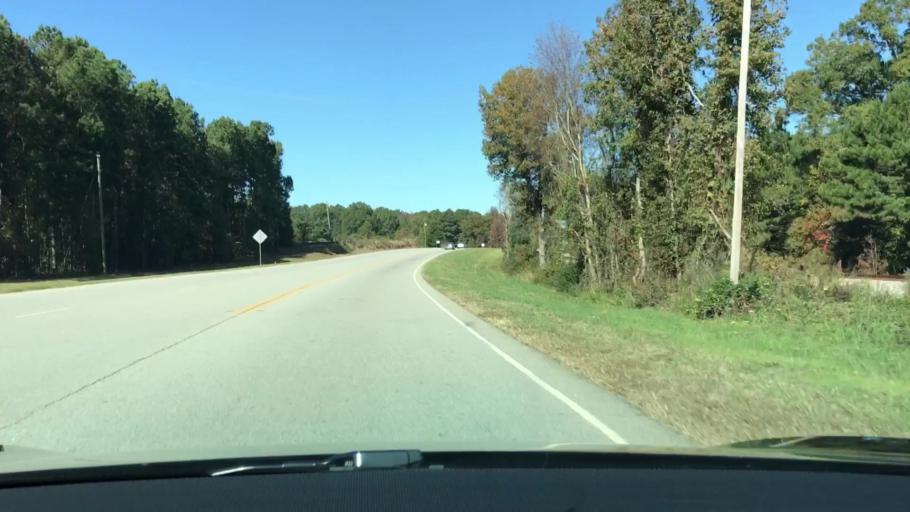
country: US
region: Georgia
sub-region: Warren County
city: Firing Range
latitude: 33.4853
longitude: -82.7937
